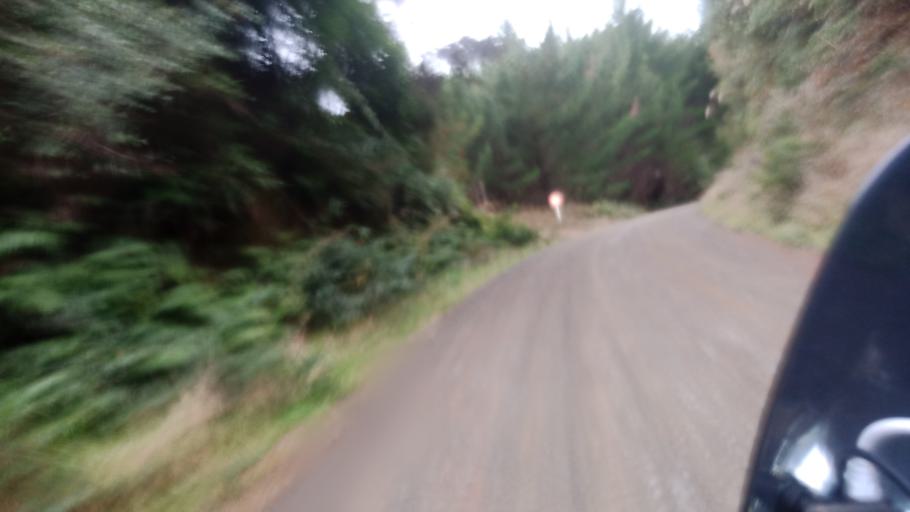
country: NZ
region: Bay of Plenty
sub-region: Whakatane District
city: Murupara
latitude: -38.6317
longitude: 176.7036
